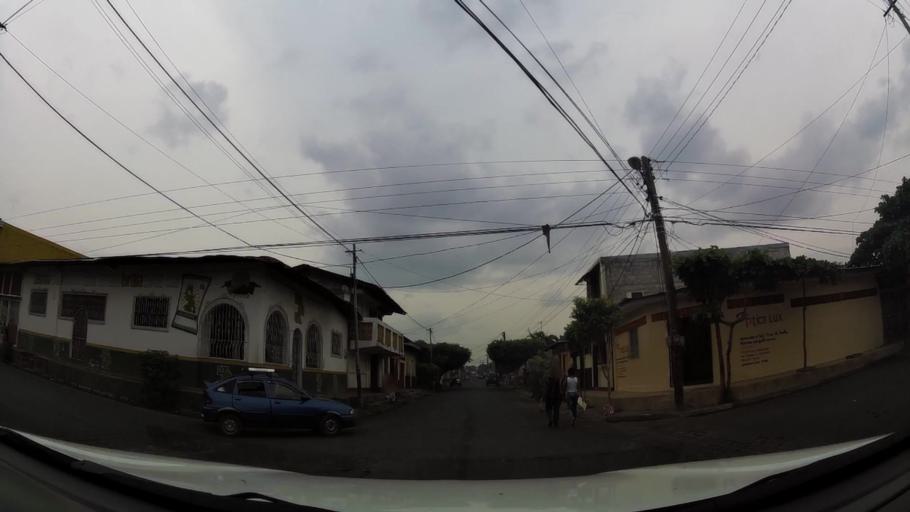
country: NI
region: Leon
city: Leon
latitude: 12.4454
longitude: -86.8760
